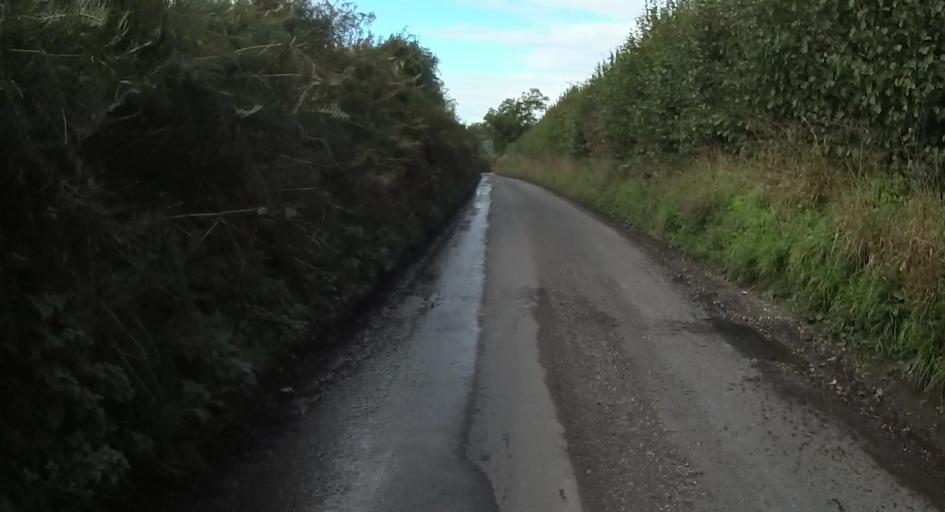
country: GB
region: England
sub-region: Hampshire
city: Kingsley
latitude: 51.1518
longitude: -0.9203
